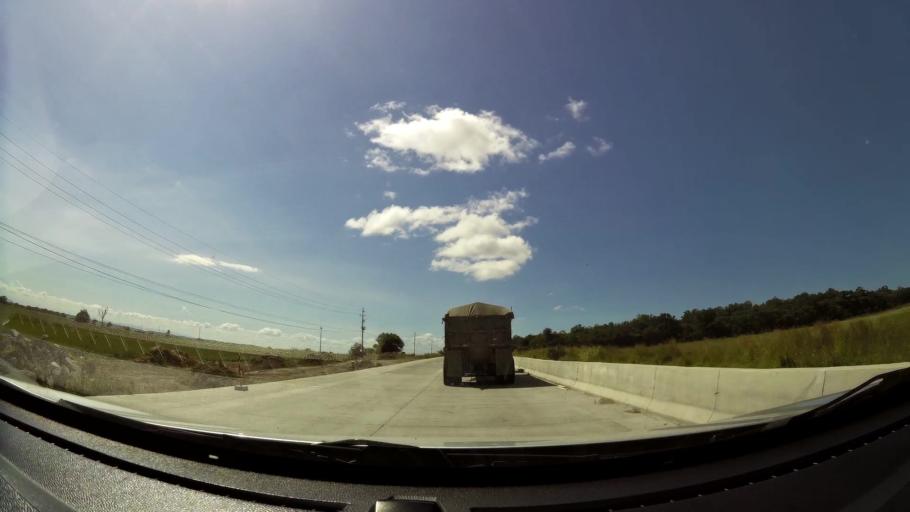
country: CR
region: Guanacaste
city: Bagaces
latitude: 10.5399
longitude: -85.3232
